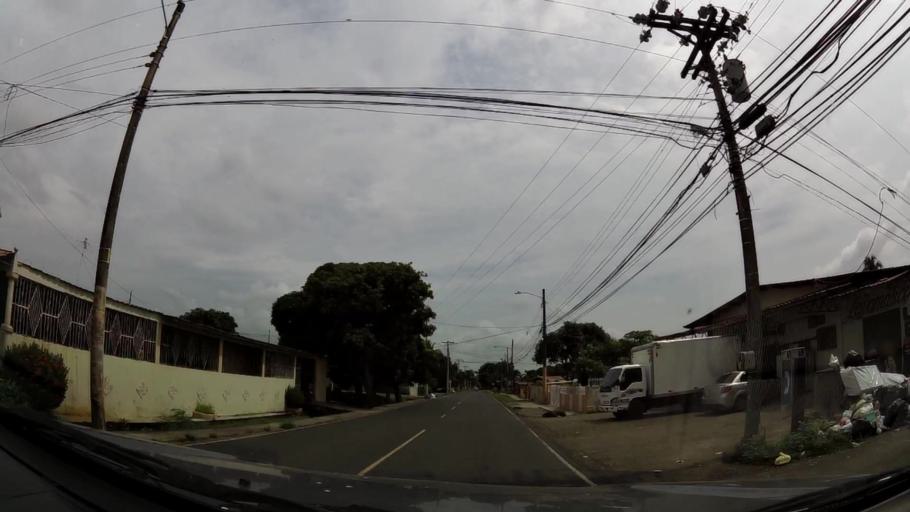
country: PA
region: Panama
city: San Miguelito
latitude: 9.0417
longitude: -79.4250
